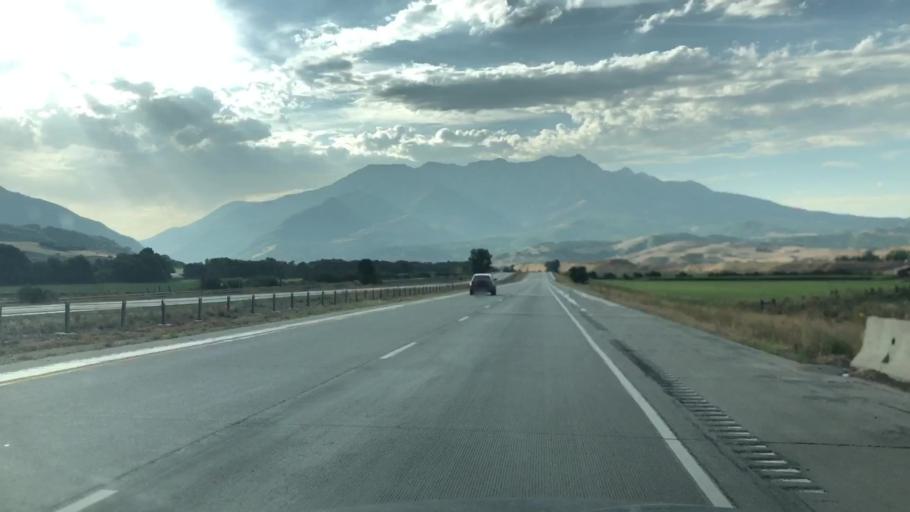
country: US
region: Utah
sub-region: Morgan County
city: Mountain Green
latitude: 41.1265
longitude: -111.7681
